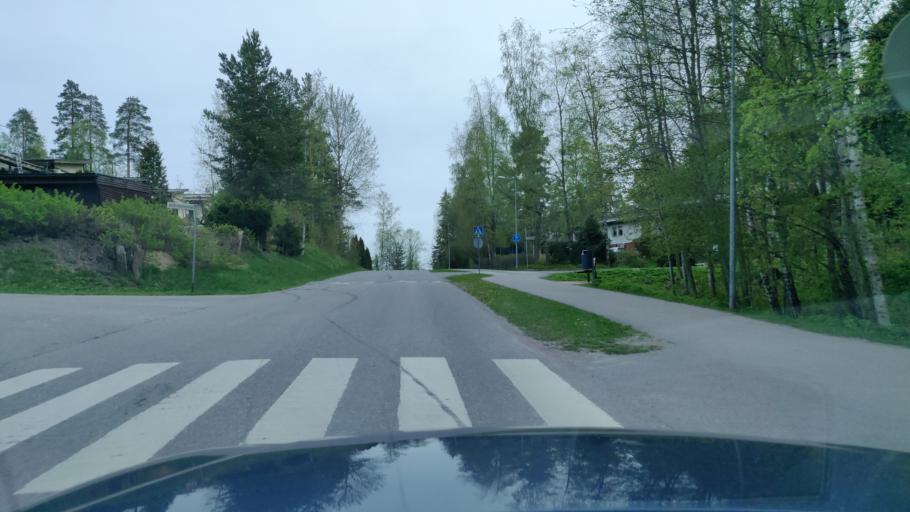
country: FI
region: Uusimaa
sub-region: Helsinki
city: Nurmijaervi
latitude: 60.3725
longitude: 24.7544
